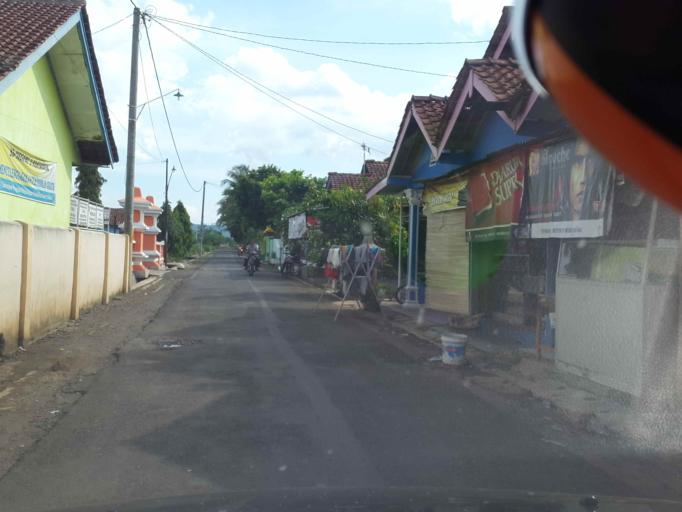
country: ID
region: Central Java
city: Purbalingga
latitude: -7.4522
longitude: 109.4984
